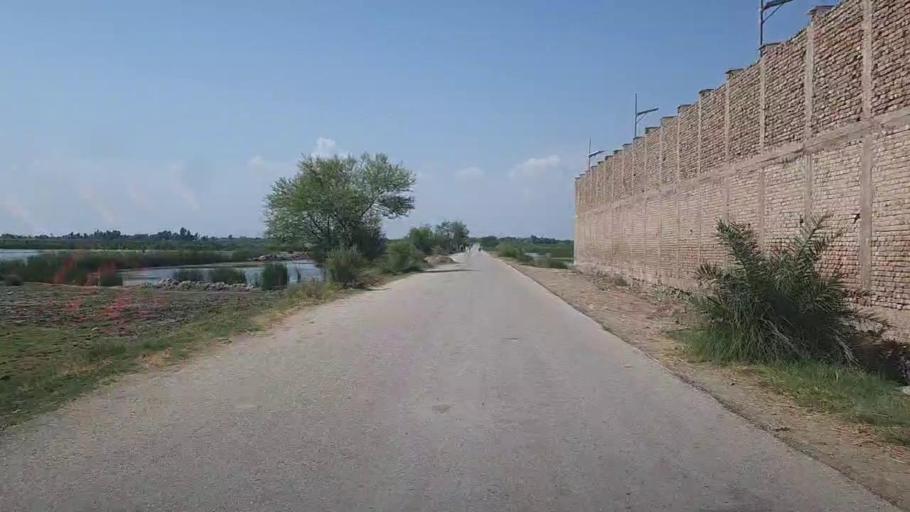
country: PK
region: Sindh
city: Khairpur
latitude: 28.0673
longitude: 69.6434
